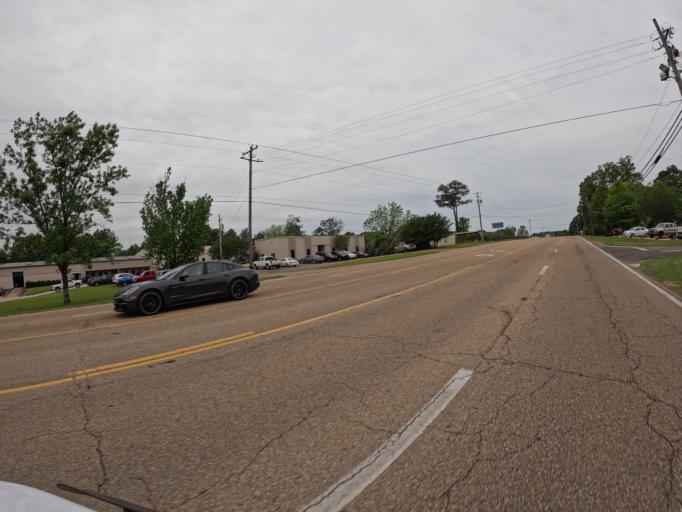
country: US
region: Mississippi
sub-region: Lee County
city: Tupelo
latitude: 34.2872
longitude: -88.7421
